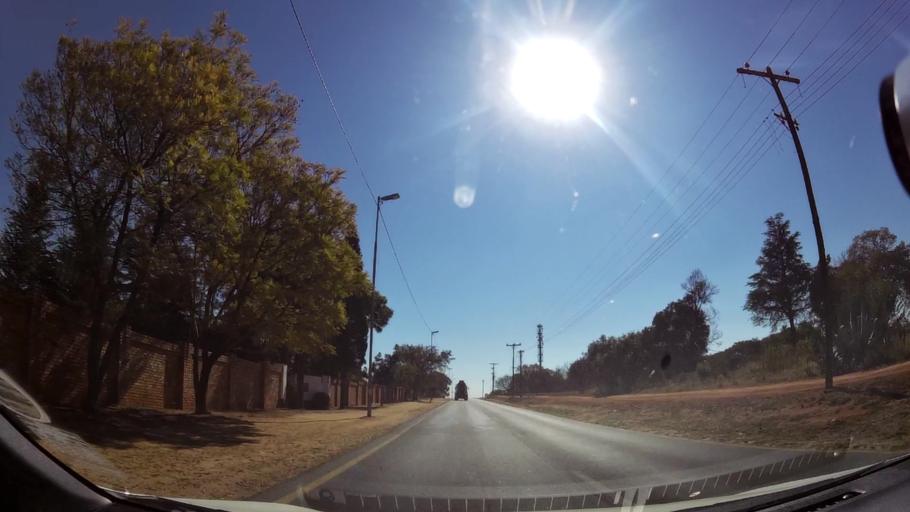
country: ZA
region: Gauteng
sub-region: City of Johannesburg Metropolitan Municipality
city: Midrand
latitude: -25.9443
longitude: 28.0970
